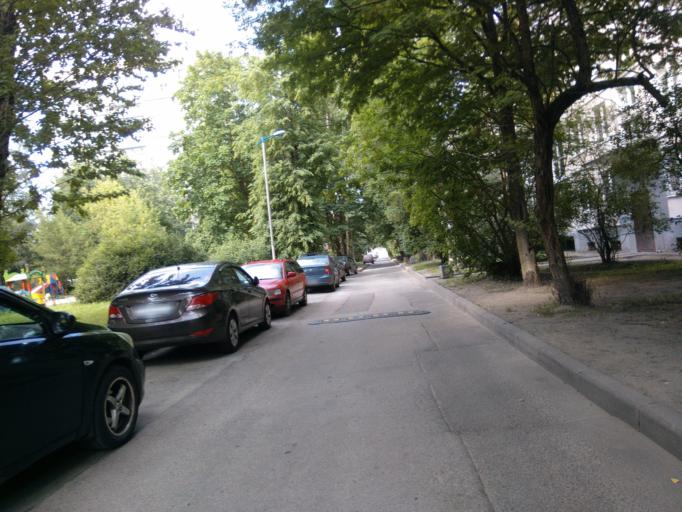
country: RU
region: Leningrad
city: Akademicheskoe
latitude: 60.0227
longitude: 30.3947
